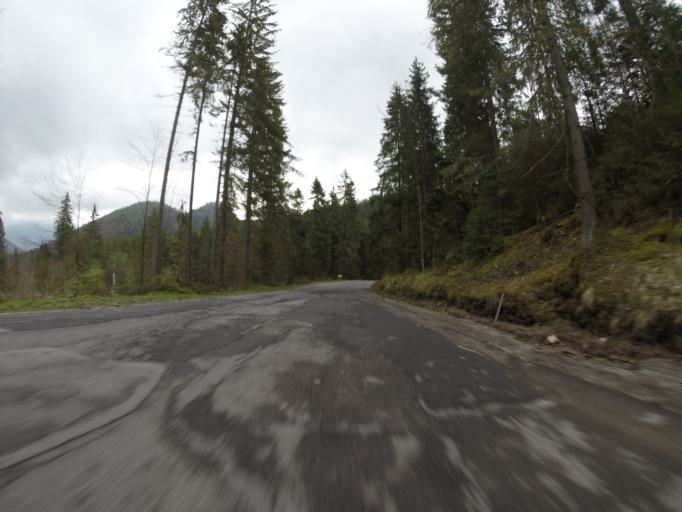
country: SK
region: Banskobystricky
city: Revuca
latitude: 48.7995
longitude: 20.1446
